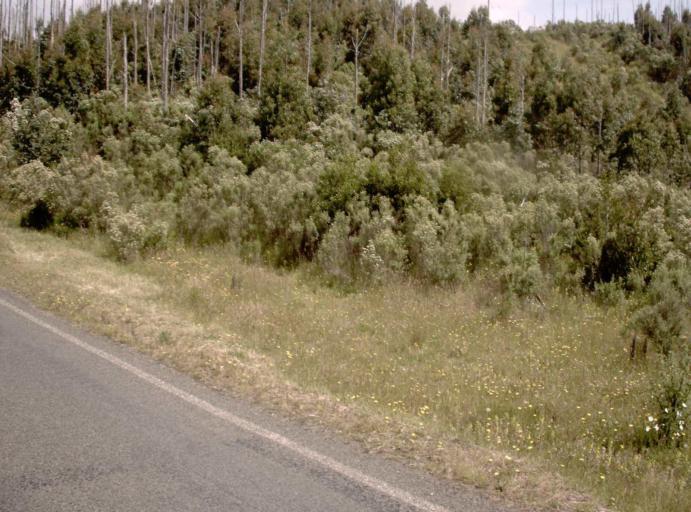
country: AU
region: Victoria
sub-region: Latrobe
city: Traralgon
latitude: -38.3676
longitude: 146.5671
